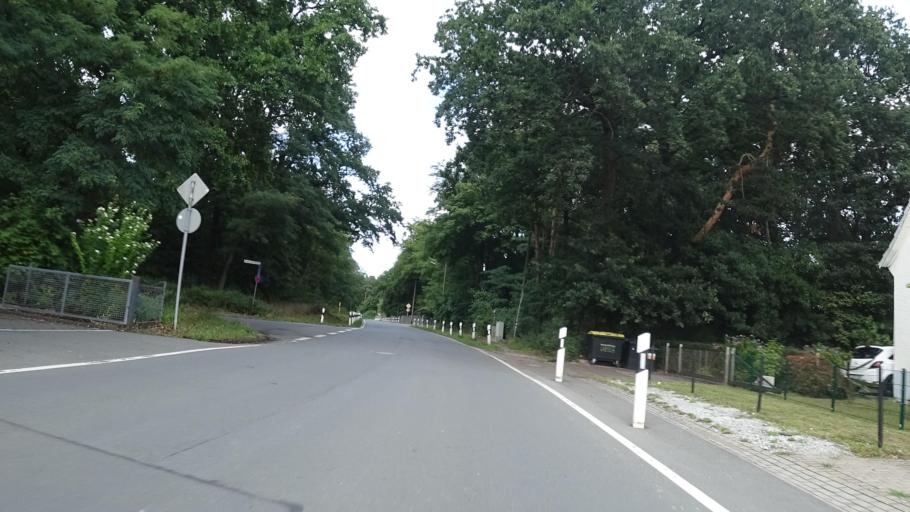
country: DE
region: North Rhine-Westphalia
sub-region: Regierungsbezirk Detmold
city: Steinhagen
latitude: 51.9666
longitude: 8.4384
